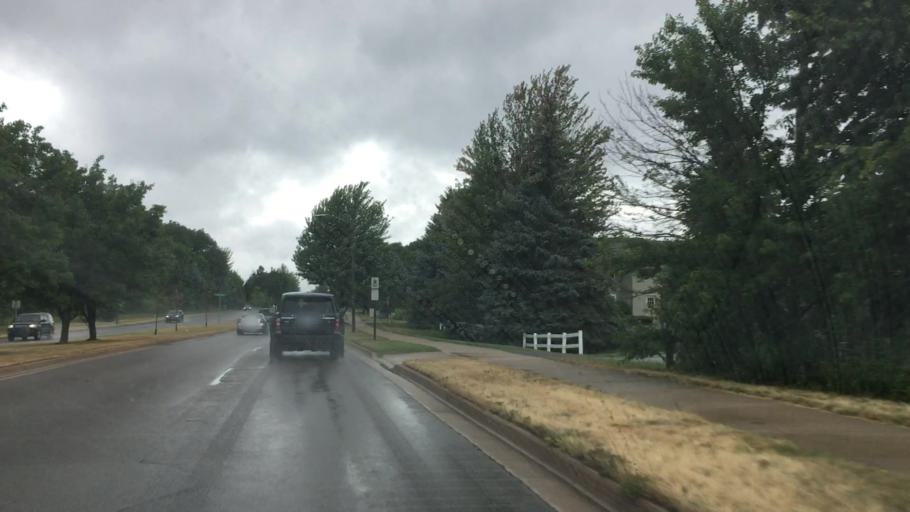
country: US
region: Michigan
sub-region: Ottawa County
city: Holland
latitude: 42.7833
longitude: -86.0651
